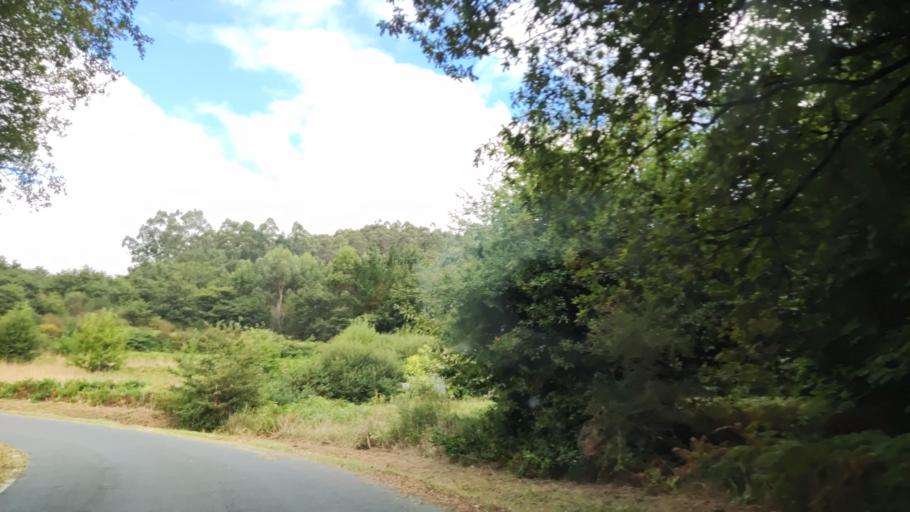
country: ES
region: Galicia
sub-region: Provincia da Coruna
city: Rois
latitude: 42.7461
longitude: -8.6979
